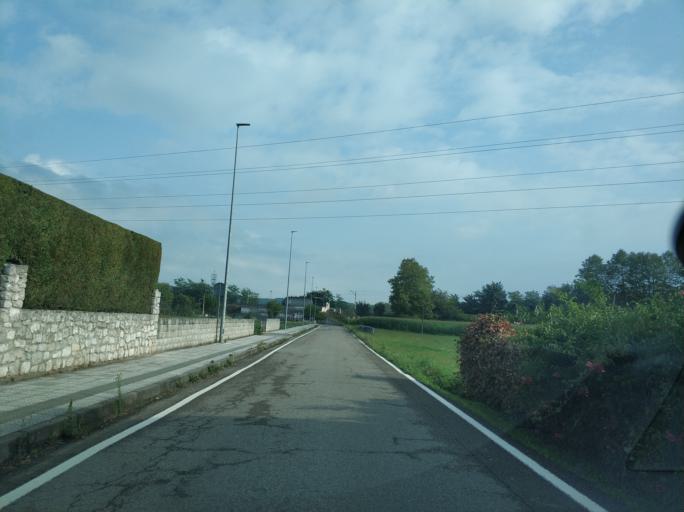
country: ES
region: Cantabria
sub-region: Provincia de Cantabria
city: Polanco
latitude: 43.3589
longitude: -3.9647
